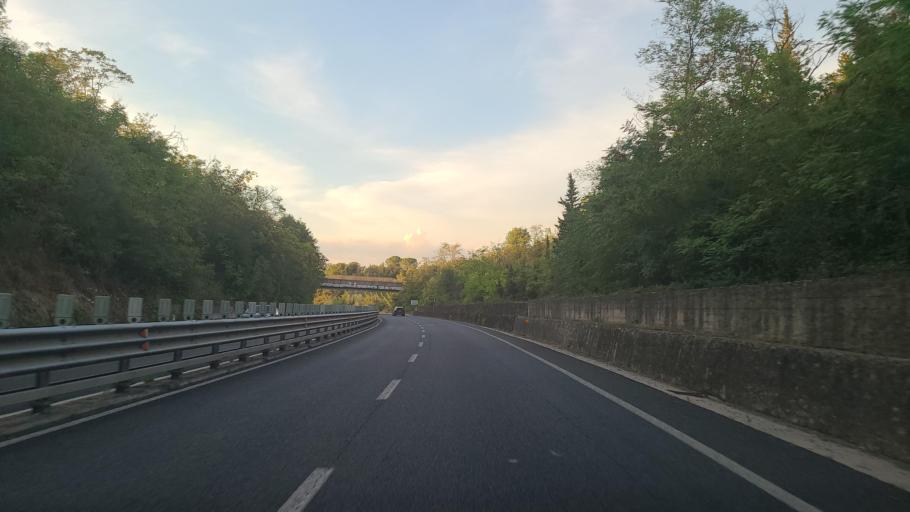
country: IT
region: Tuscany
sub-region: Province of Florence
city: Sambuca
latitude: 43.5366
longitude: 11.2204
